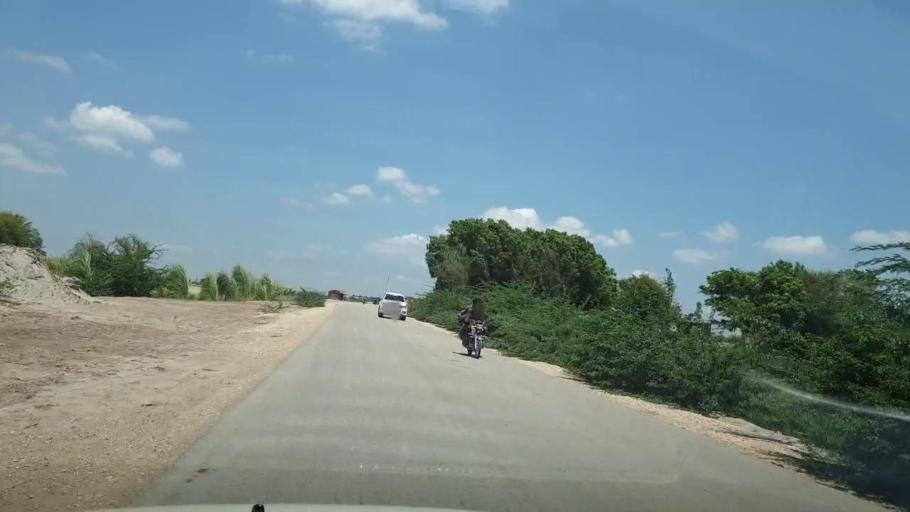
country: PK
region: Sindh
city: Sanghar
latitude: 26.0683
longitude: 69.0055
